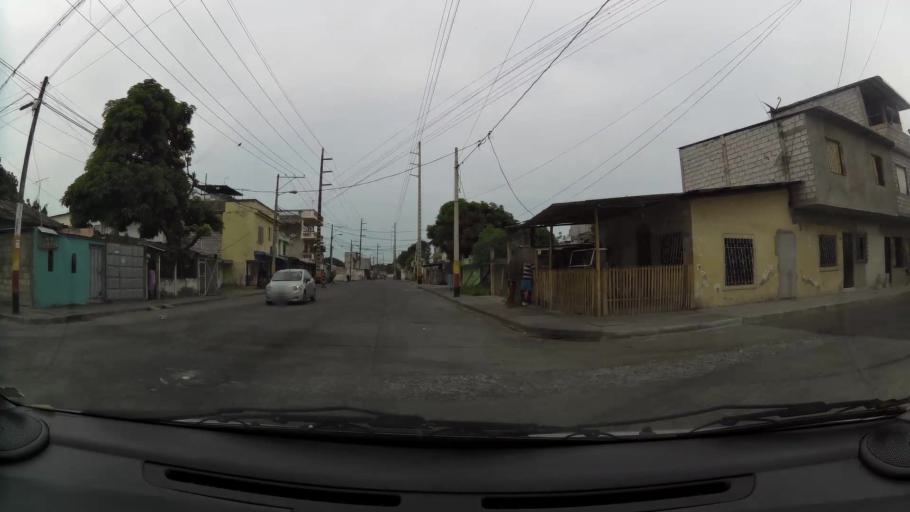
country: EC
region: Guayas
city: Guayaquil
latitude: -2.2566
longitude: -79.8748
